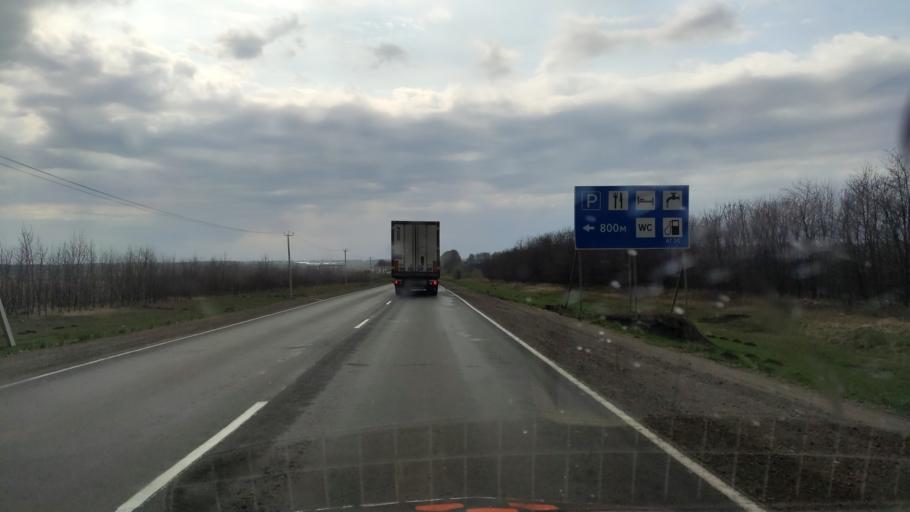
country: RU
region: Voronezj
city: Nizhnedevitsk
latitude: 51.5665
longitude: 38.2711
